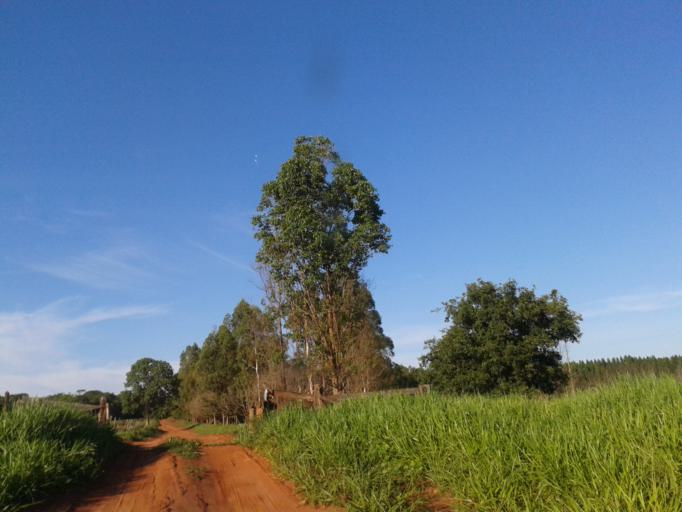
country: BR
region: Minas Gerais
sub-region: Santa Vitoria
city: Santa Vitoria
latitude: -18.9680
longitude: -49.8805
